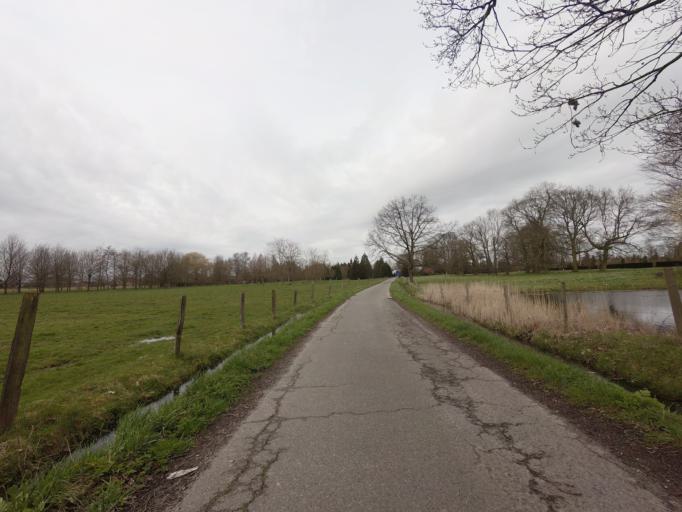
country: BE
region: Flanders
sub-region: Provincie Antwerpen
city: Lier
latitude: 51.1196
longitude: 4.5461
